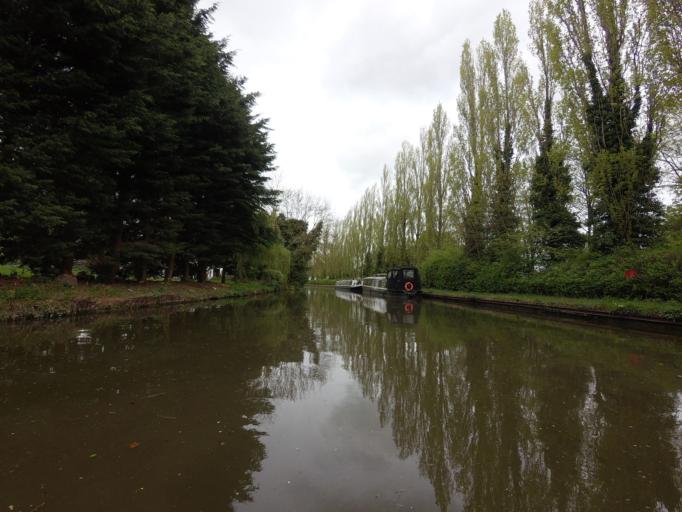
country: GB
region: England
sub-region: Milton Keynes
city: Simpson
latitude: 52.0188
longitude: -0.7182
